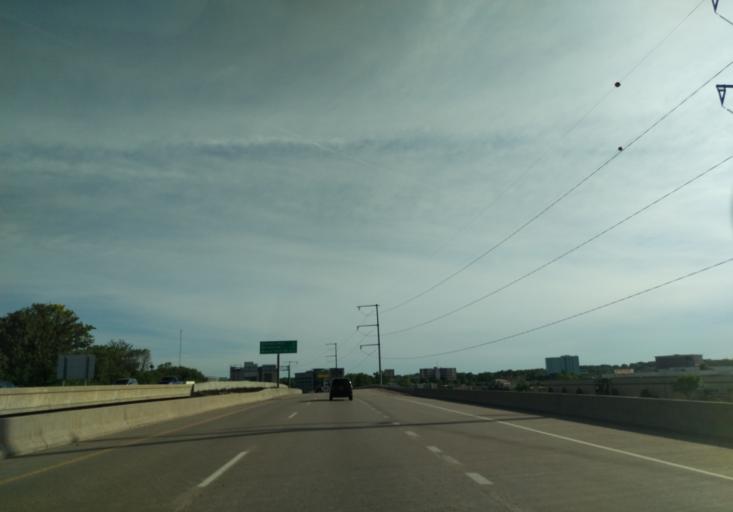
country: US
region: Wisconsin
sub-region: Dane County
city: Middleton
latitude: 43.0955
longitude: -89.5178
